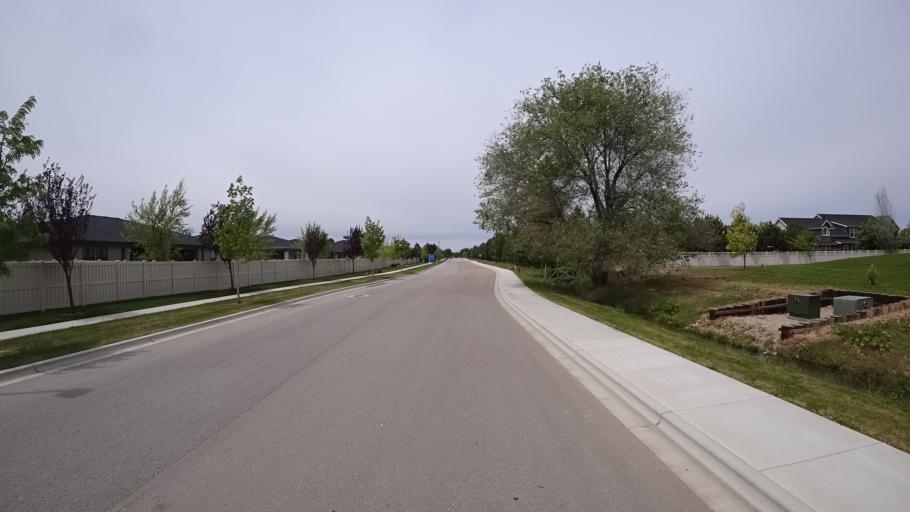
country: US
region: Idaho
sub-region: Ada County
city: Meridian
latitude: 43.5665
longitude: -116.3501
